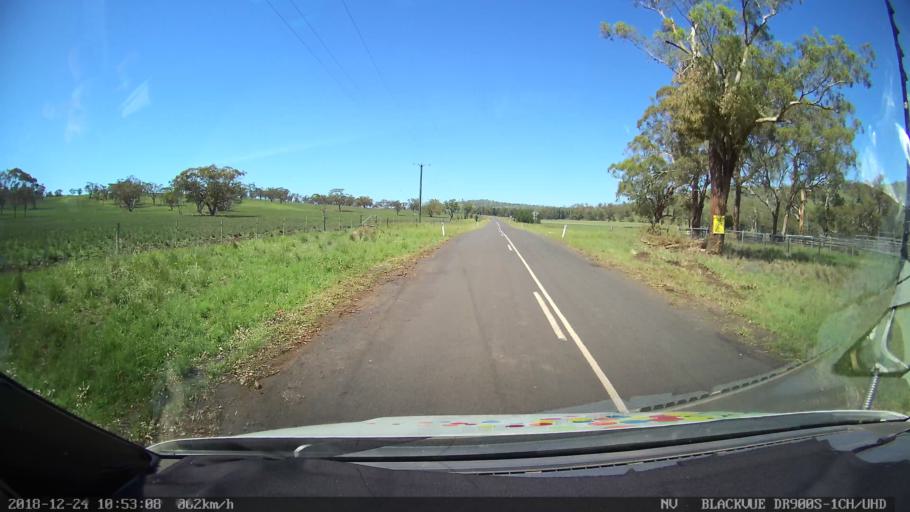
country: AU
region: New South Wales
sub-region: Upper Hunter Shire
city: Merriwa
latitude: -31.9886
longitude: 150.4228
